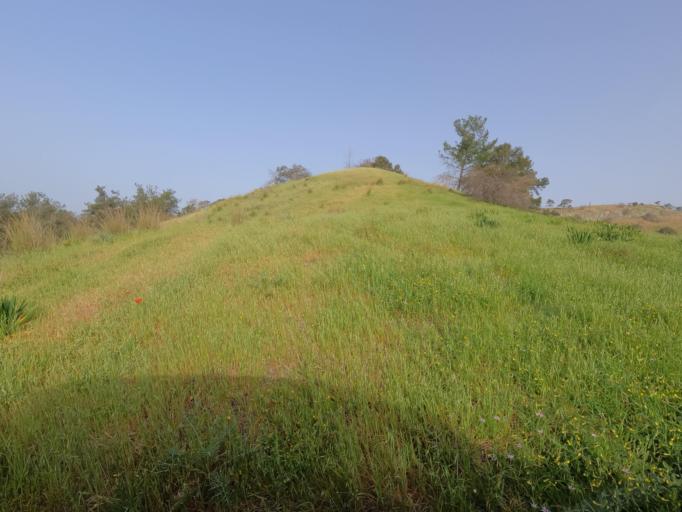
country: CY
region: Pafos
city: Polis
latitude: 34.9910
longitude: 32.3315
